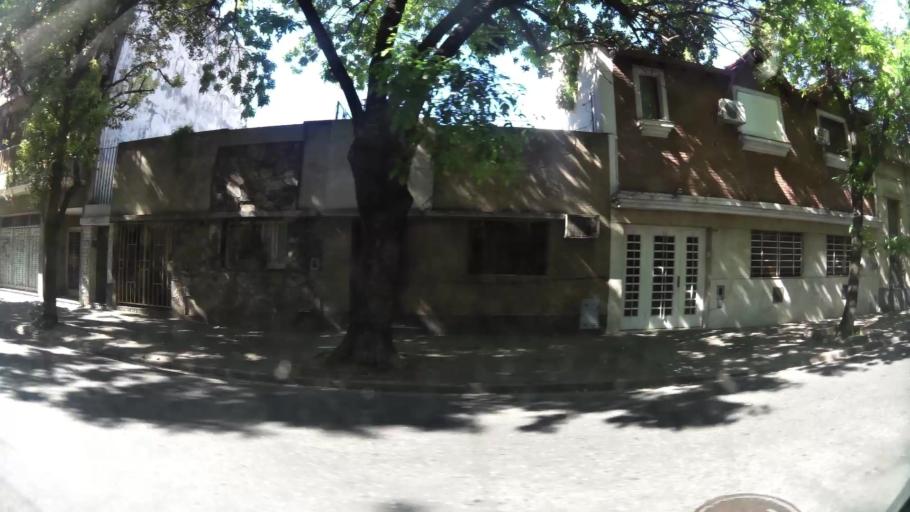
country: AR
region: Santa Fe
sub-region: Departamento de Rosario
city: Rosario
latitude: -32.9437
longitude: -60.6754
